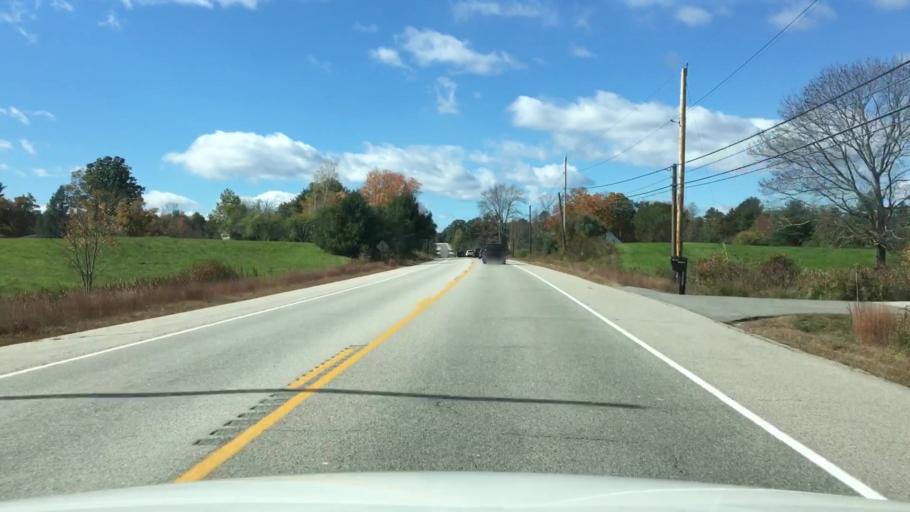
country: US
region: Maine
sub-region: York County
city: West Kennebunk
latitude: 43.4781
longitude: -70.5676
